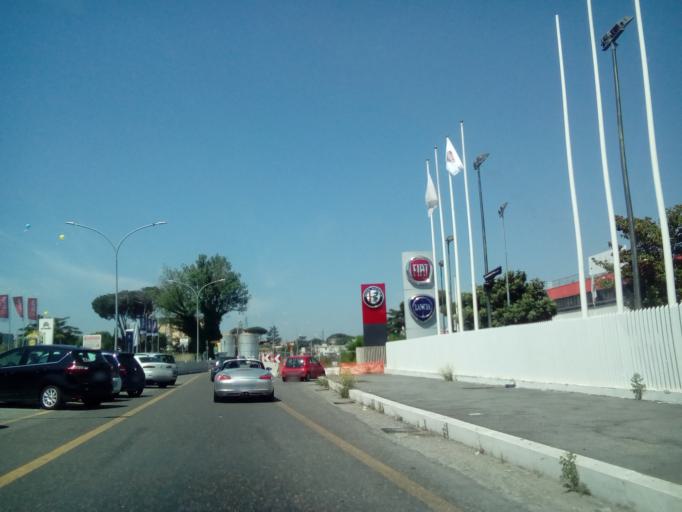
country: IT
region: Latium
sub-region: Citta metropolitana di Roma Capitale
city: Colle Verde
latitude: 41.9327
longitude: 12.5954
